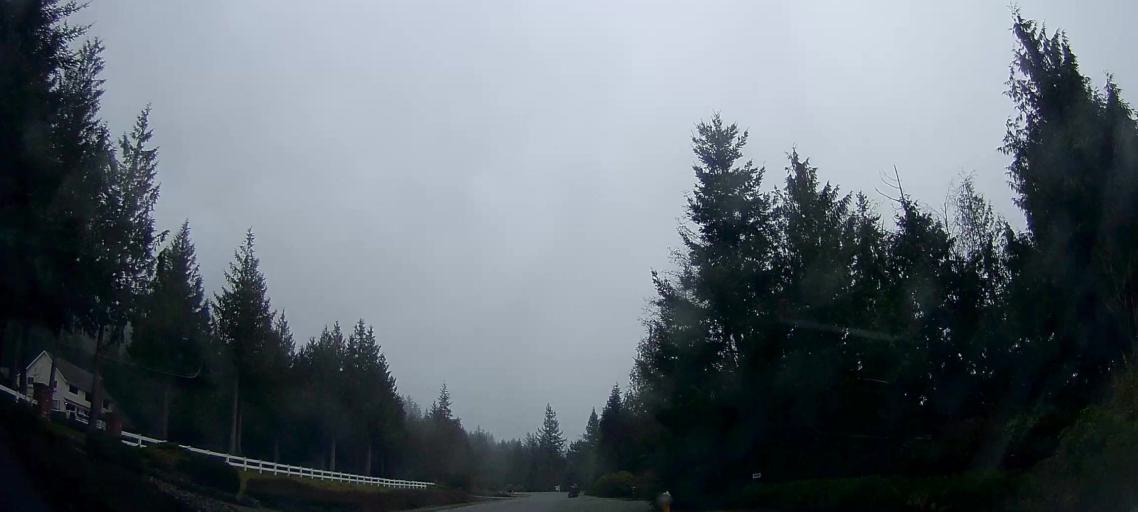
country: US
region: Washington
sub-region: Skagit County
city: Big Lake
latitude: 48.3760
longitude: -122.2945
